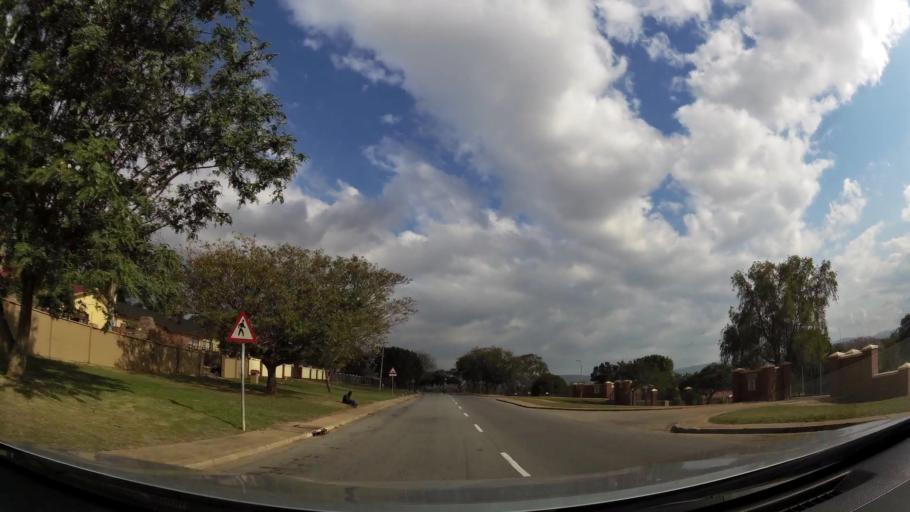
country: ZA
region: Eastern Cape
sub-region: Nelson Mandela Bay Metropolitan Municipality
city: Uitenhage
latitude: -33.7374
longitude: 25.4052
